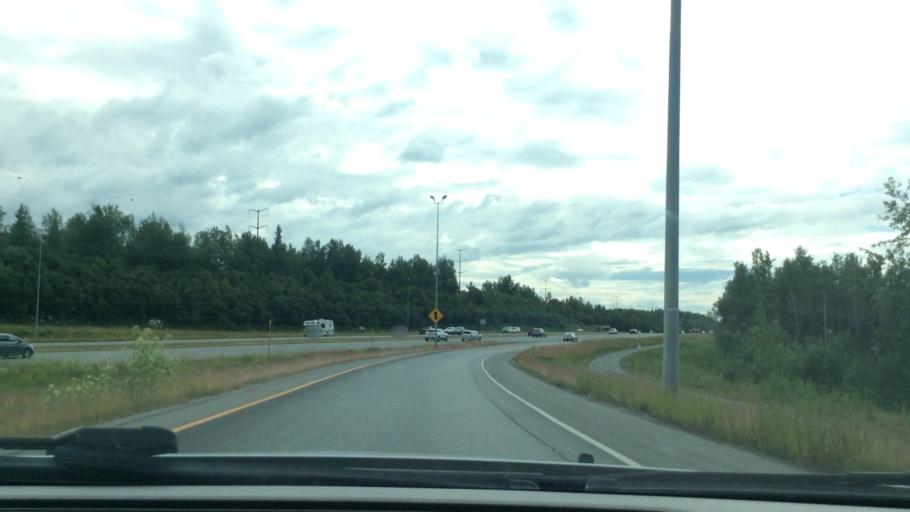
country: US
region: Alaska
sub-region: Anchorage Municipality
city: Elmendorf Air Force Base
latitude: 61.2532
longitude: -149.6618
